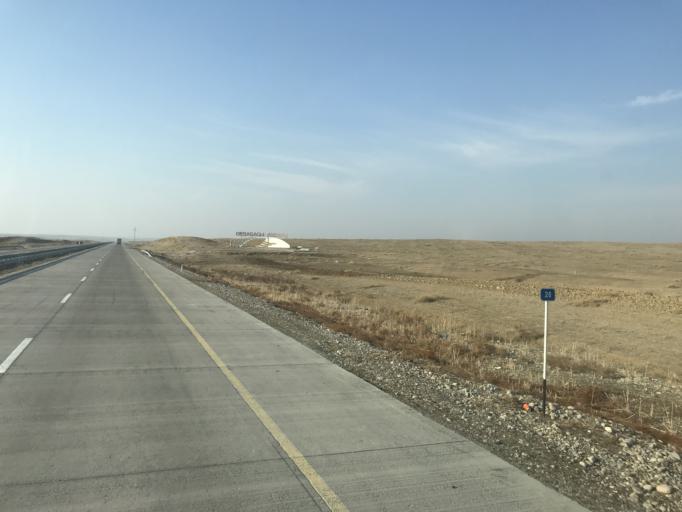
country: KZ
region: Ongtustik Qazaqstan
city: Temirlanovka
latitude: 42.5158
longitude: 69.4272
